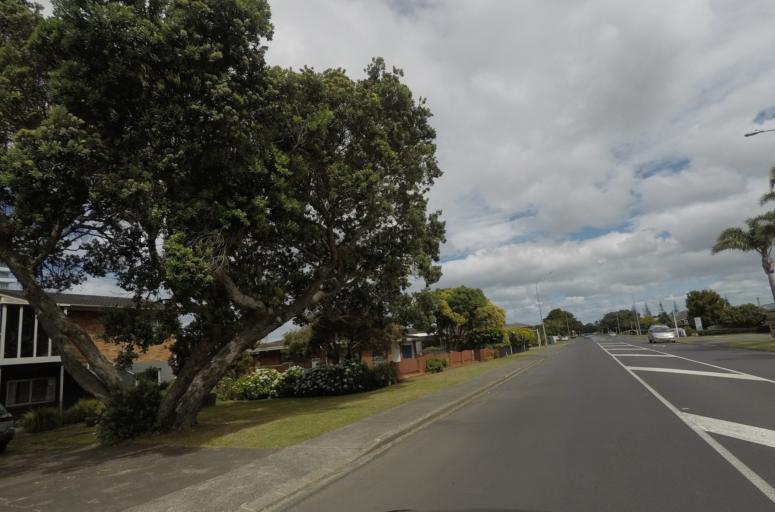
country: NZ
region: Auckland
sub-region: Auckland
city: Rothesay Bay
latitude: -36.5876
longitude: 174.6924
